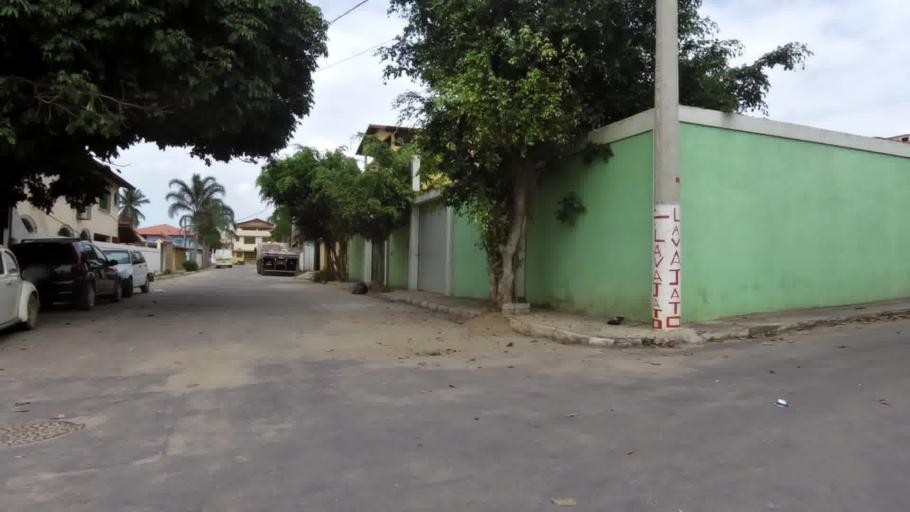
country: BR
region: Espirito Santo
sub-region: Marataizes
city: Marataizes
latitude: -21.0363
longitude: -40.8187
